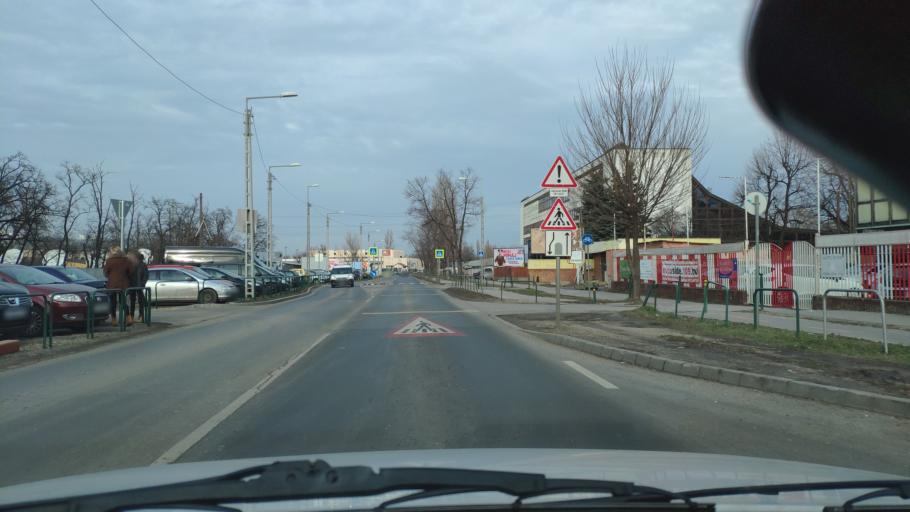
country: HU
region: Budapest
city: Budapest XIX. keruelet
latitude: 47.4671
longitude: 19.1268
